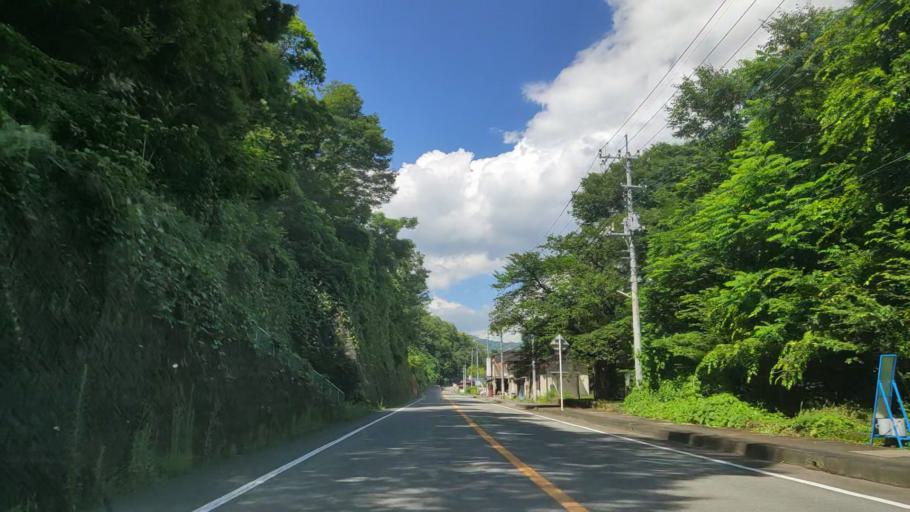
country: JP
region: Yamanashi
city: Enzan
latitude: 35.7228
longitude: 138.7057
